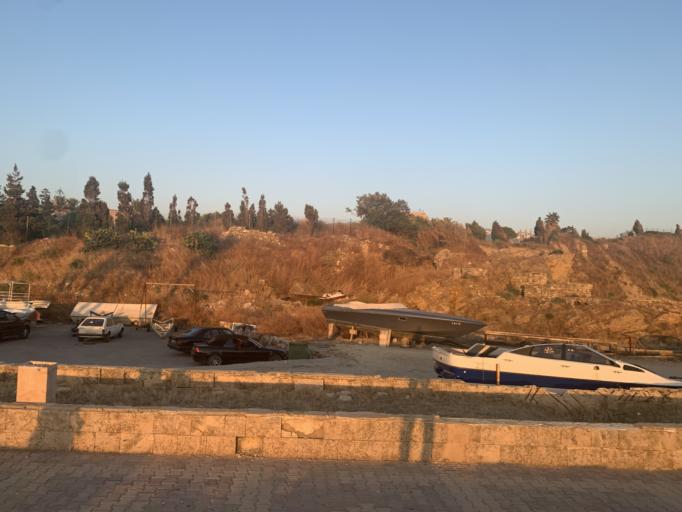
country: LB
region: Mont-Liban
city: Jbail
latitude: 34.1205
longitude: 35.6433
